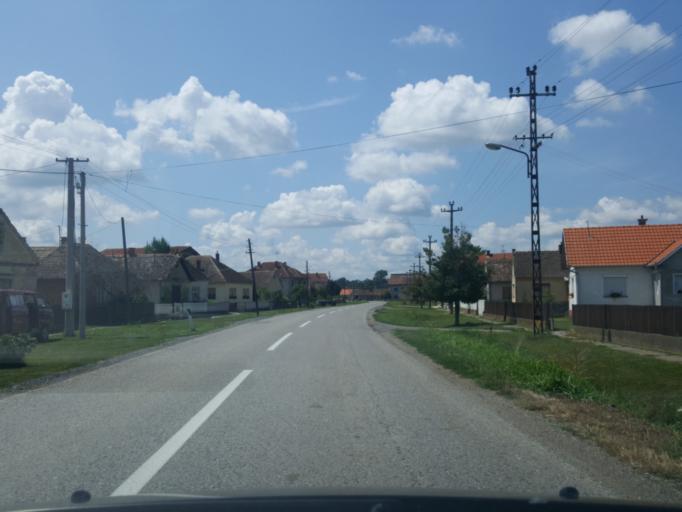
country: RS
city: Metkovic
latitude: 44.8533
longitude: 19.5377
